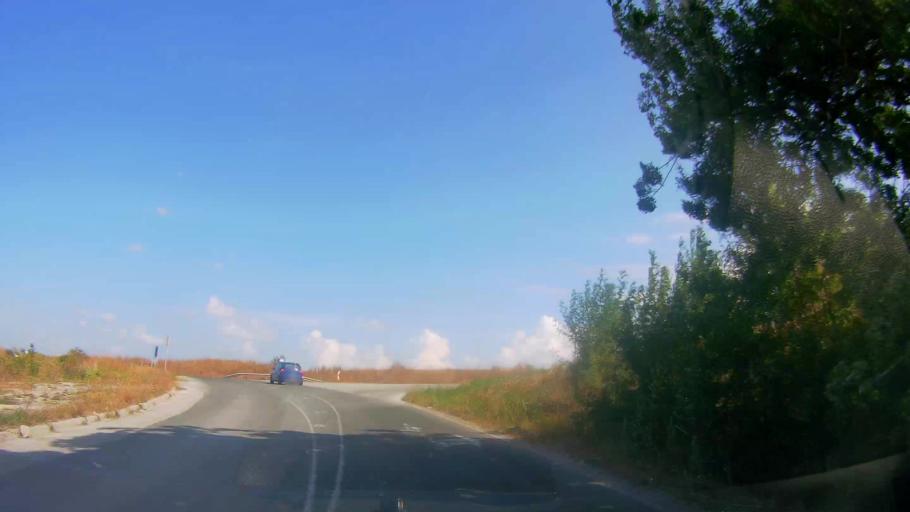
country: BG
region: Burgas
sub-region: Obshtina Burgas
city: Burgas
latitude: 42.4736
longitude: 27.3622
